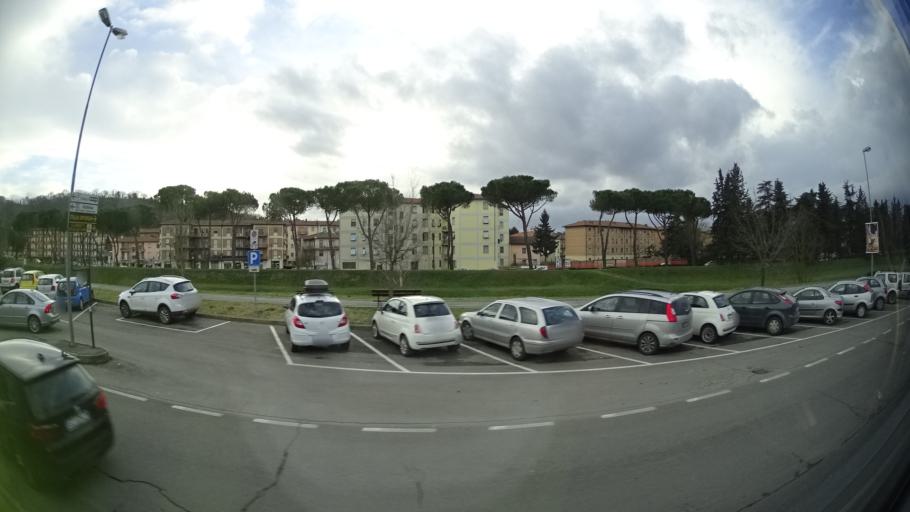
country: IT
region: Tuscany
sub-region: Provincia di Siena
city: Poggibonsi
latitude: 43.4687
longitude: 11.1533
